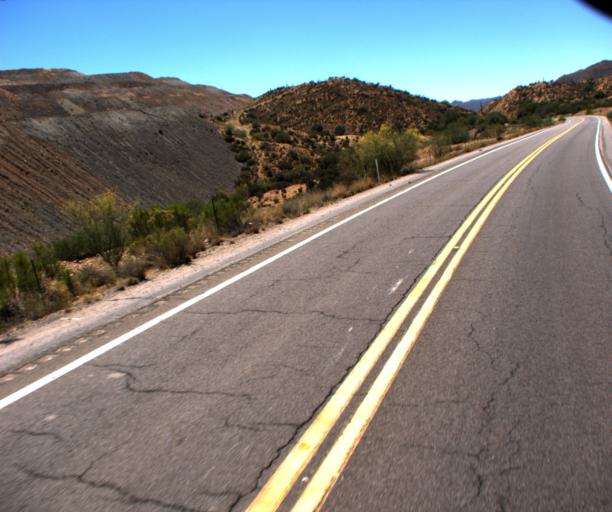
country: US
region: Arizona
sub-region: Pinal County
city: Kearny
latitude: 33.1583
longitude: -110.9968
